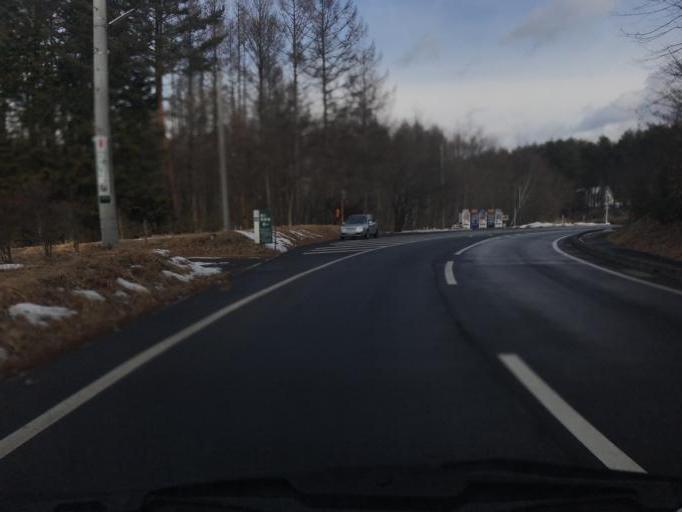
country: JP
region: Nagano
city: Chino
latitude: 35.8819
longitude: 138.3086
